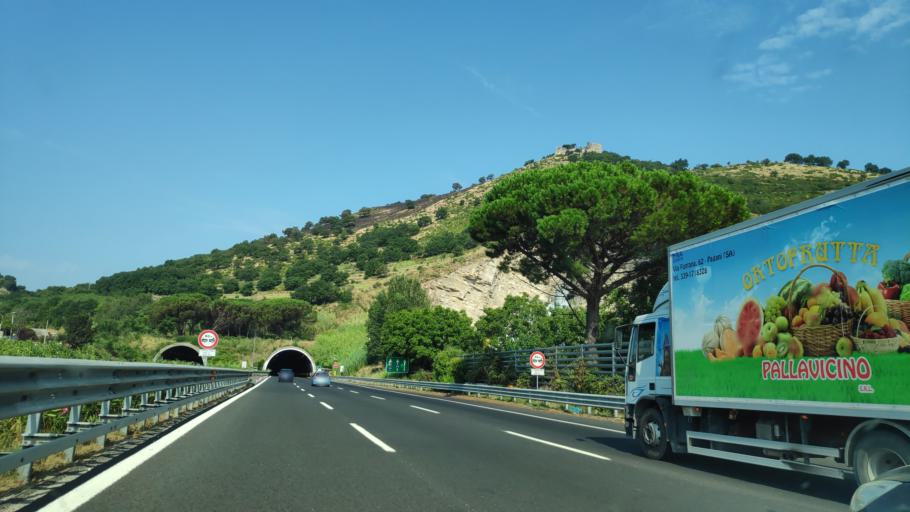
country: IT
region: Campania
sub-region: Provincia di Salerno
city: Lanzara
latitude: 40.7721
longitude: 14.6628
